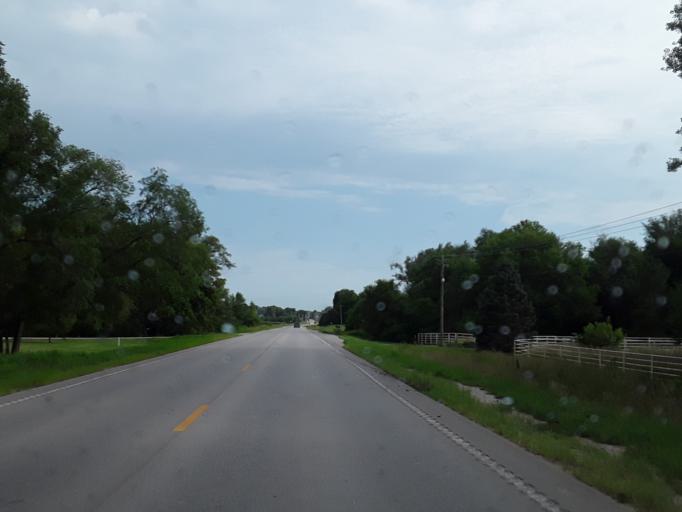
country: US
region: Nebraska
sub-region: Saunders County
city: Ashland
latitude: 41.0531
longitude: -96.3680
